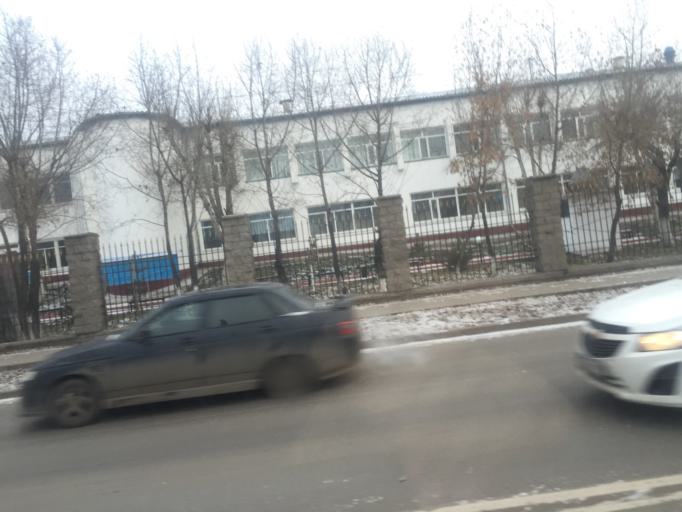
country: KZ
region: Astana Qalasy
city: Astana
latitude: 51.1951
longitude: 71.3966
